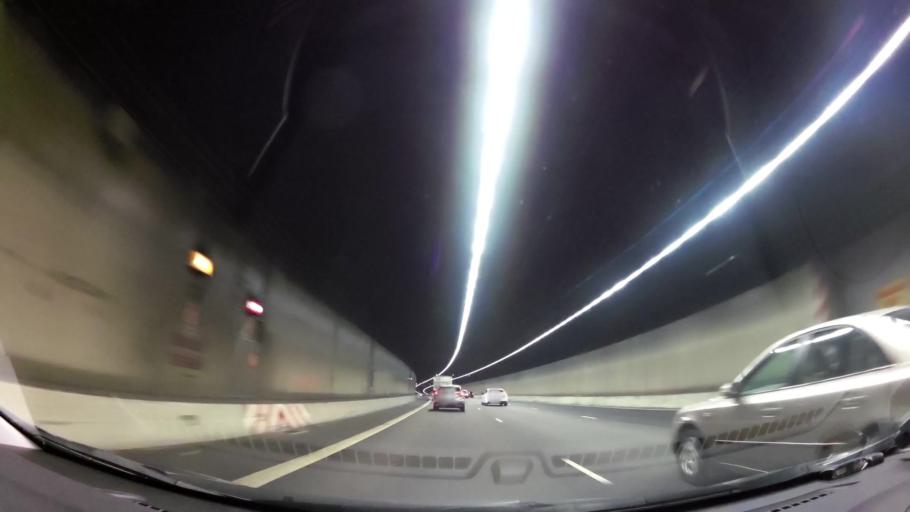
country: SG
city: Singapore
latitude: 1.2905
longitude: 103.8394
